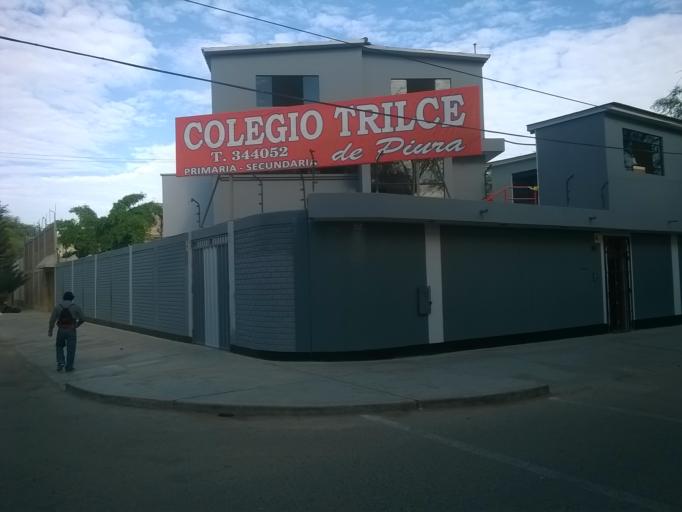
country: PE
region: Piura
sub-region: Provincia de Piura
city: Piura
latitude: -5.1872
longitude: -80.6200
